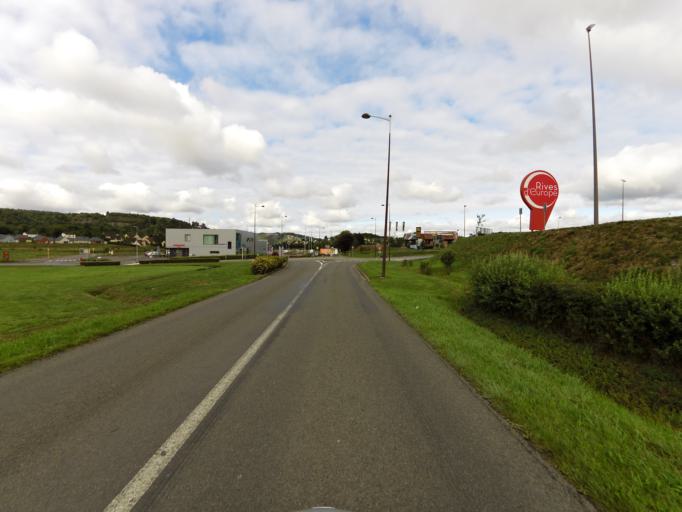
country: FR
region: Champagne-Ardenne
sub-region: Departement des Ardennes
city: Fromelennes
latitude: 50.1335
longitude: 4.8530
